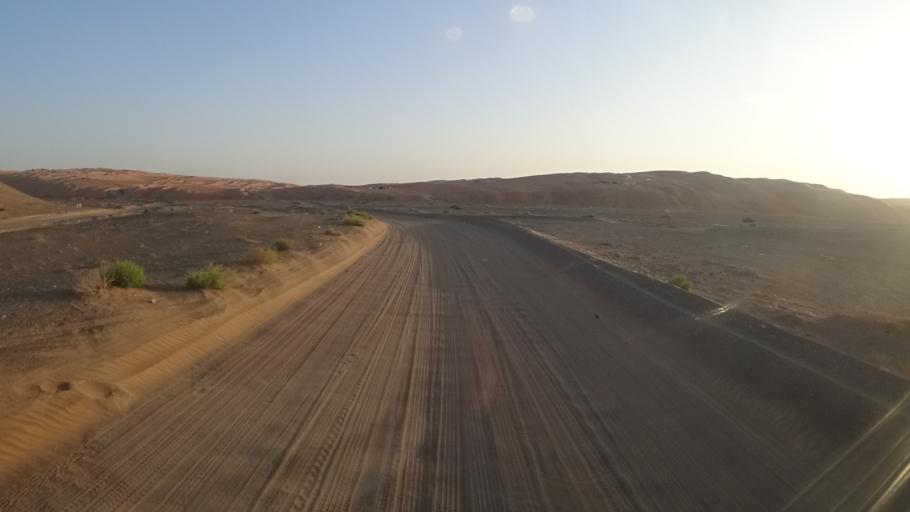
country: OM
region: Ash Sharqiyah
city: Al Qabil
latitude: 22.4958
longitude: 58.7296
